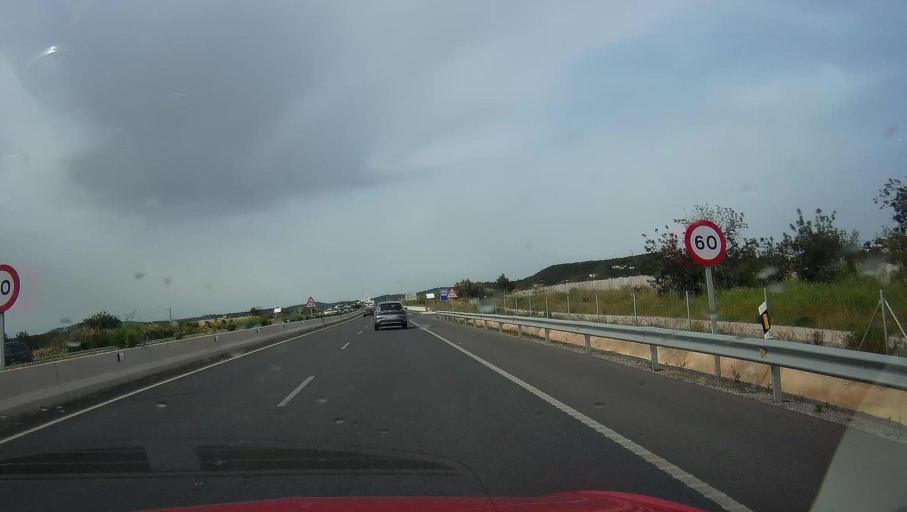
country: ES
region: Balearic Islands
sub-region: Illes Balears
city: Ibiza
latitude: 38.9396
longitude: 1.4444
